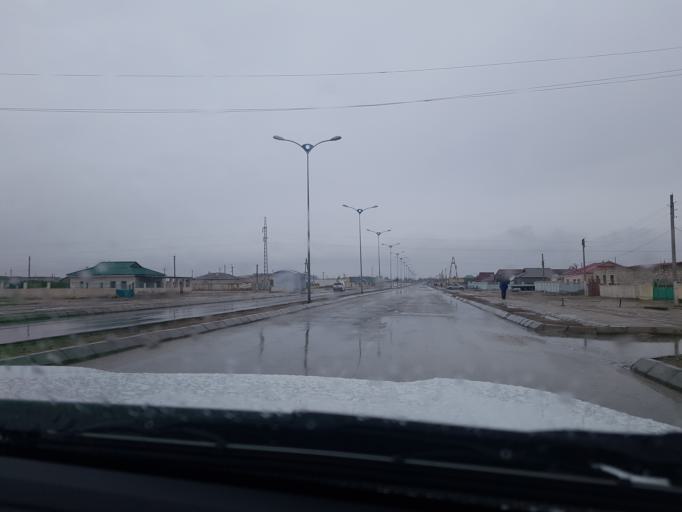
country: TM
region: Balkan
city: Balkanabat
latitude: 39.6331
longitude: 54.2435
